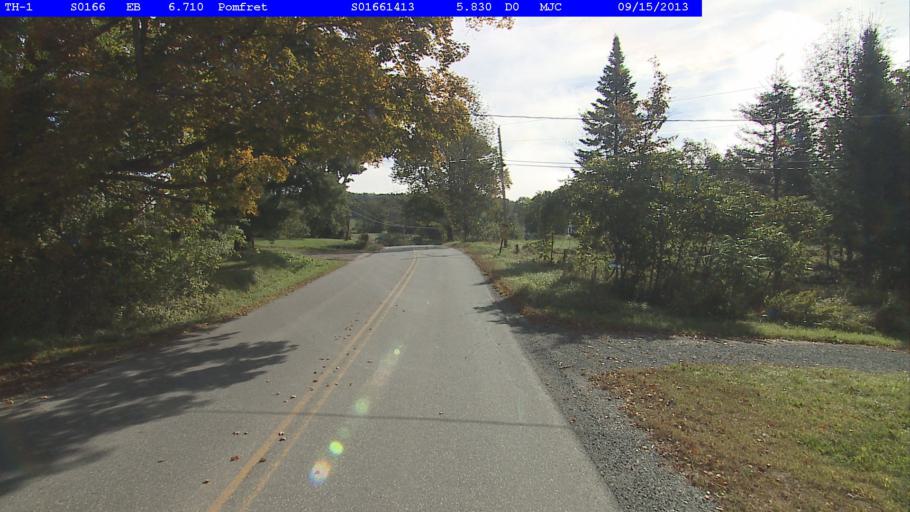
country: US
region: Vermont
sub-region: Windsor County
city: Woodstock
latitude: 43.7231
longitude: -72.5001
